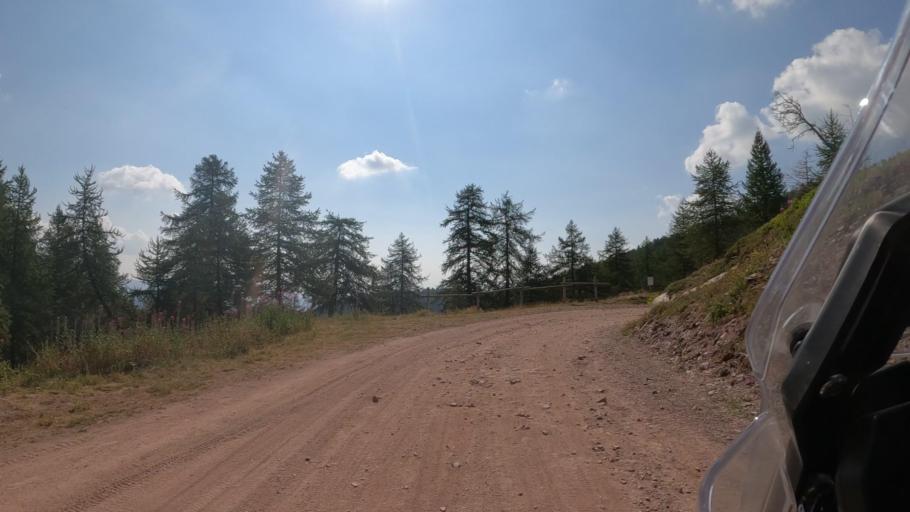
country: IT
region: Piedmont
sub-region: Provincia di Cuneo
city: Briga Alta
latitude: 44.1164
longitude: 7.6987
